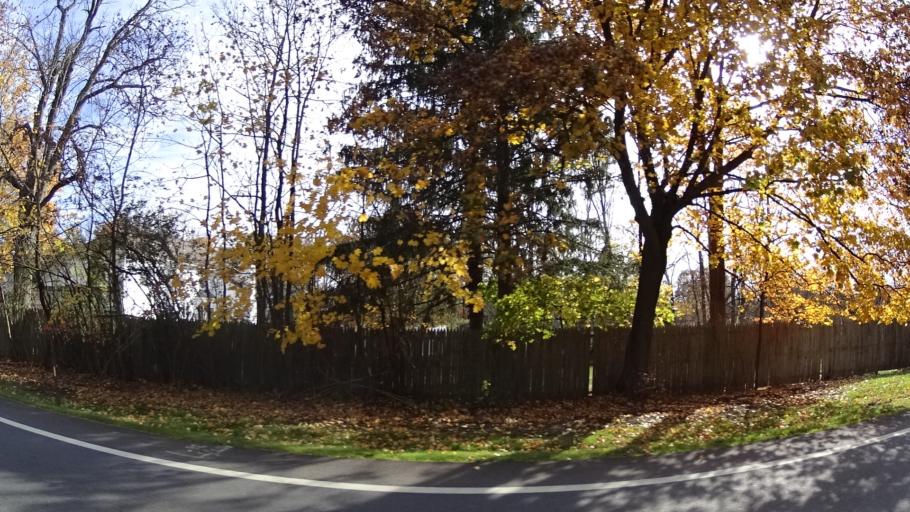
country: US
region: New Jersey
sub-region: Morris County
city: Mendham
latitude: 40.7839
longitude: -74.5810
